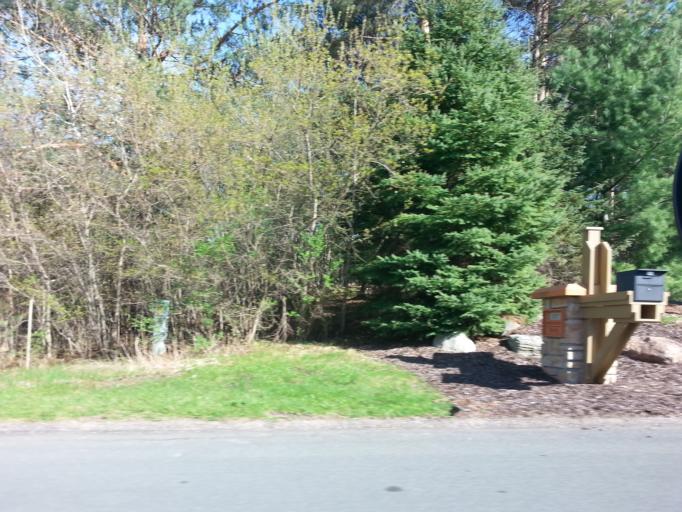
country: US
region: Minnesota
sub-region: Washington County
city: Lake Elmo
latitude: 44.9830
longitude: -92.8503
